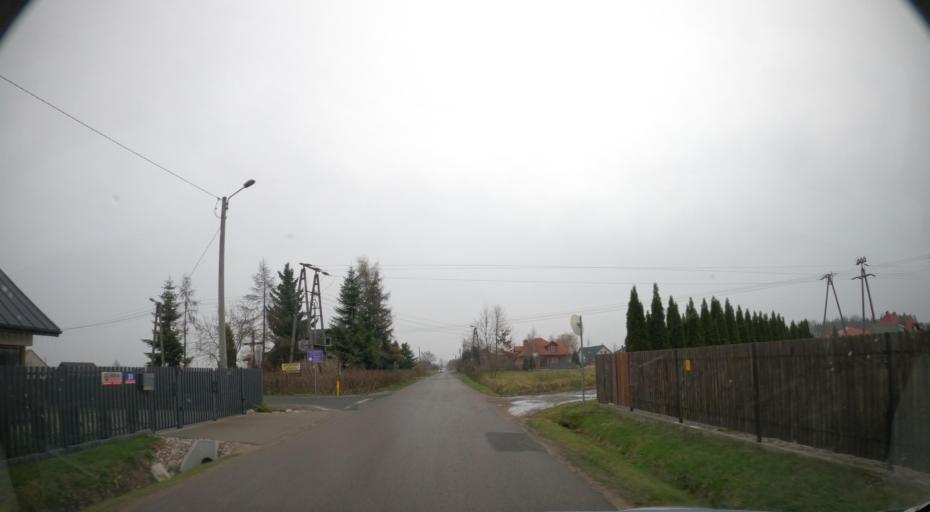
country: PL
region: Masovian Voivodeship
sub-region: Powiat radomski
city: Jastrzebia
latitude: 51.4238
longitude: 21.2386
